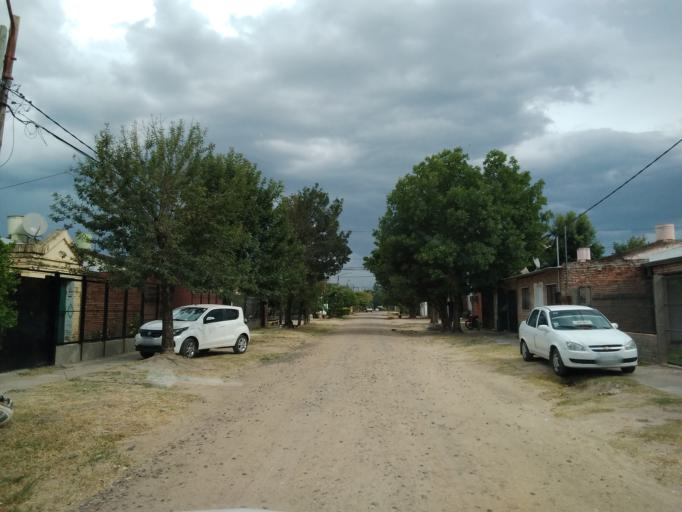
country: AR
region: Corrientes
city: Corrientes
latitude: -27.5214
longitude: -58.7936
